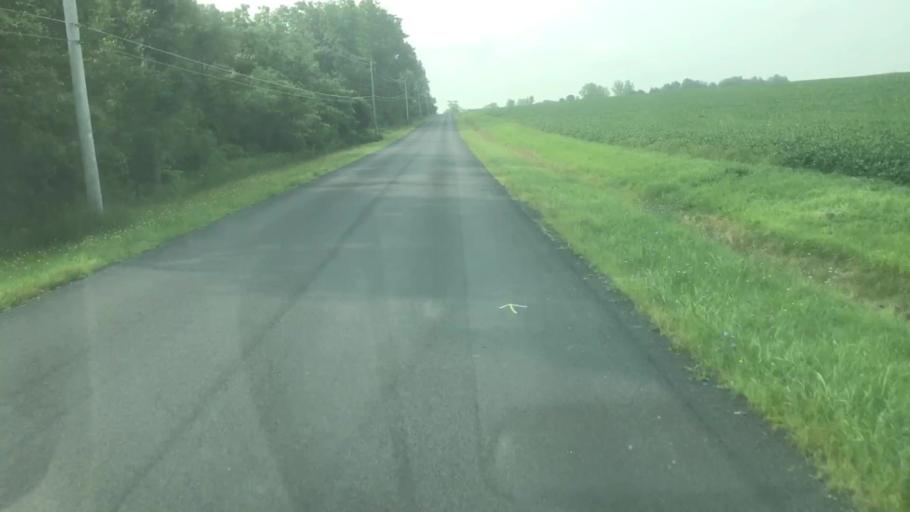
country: US
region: New York
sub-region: Onondaga County
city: Skaneateles
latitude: 42.9375
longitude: -76.4580
